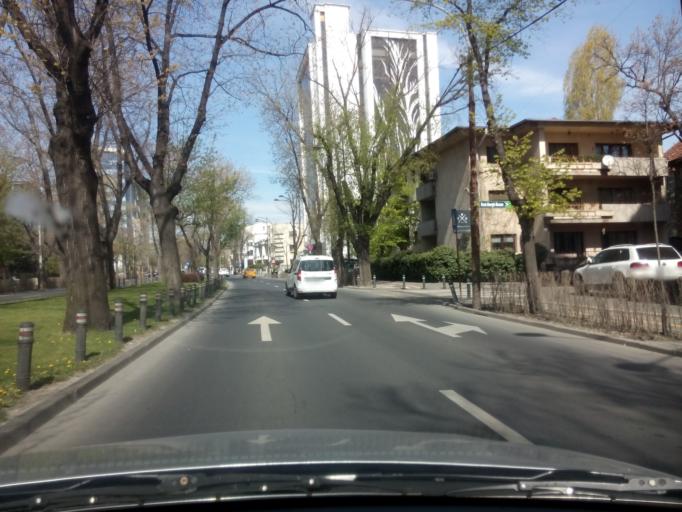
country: RO
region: Bucuresti
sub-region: Municipiul Bucuresti
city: Bucharest
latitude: 44.4634
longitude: 26.0916
